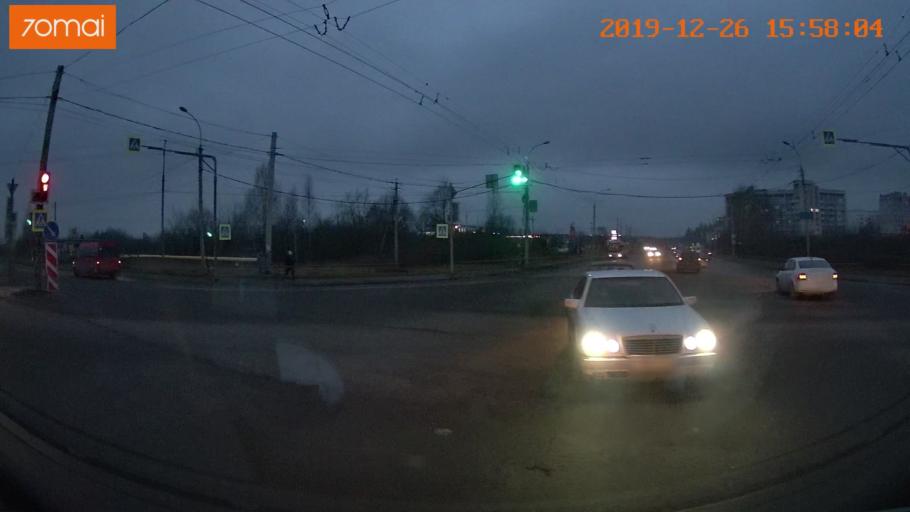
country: RU
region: Jaroslavl
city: Rybinsk
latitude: 58.0420
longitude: 38.7949
